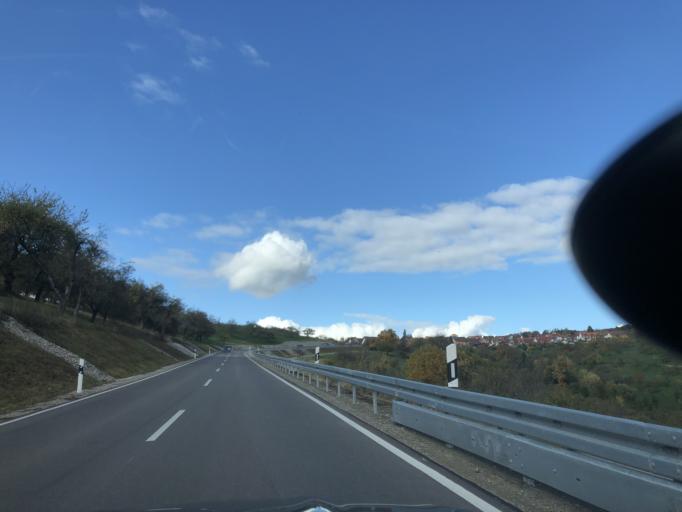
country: DE
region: Baden-Wuerttemberg
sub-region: Regierungsbezirk Stuttgart
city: Allmersbach im Tal
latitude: 48.8819
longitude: 9.4687
